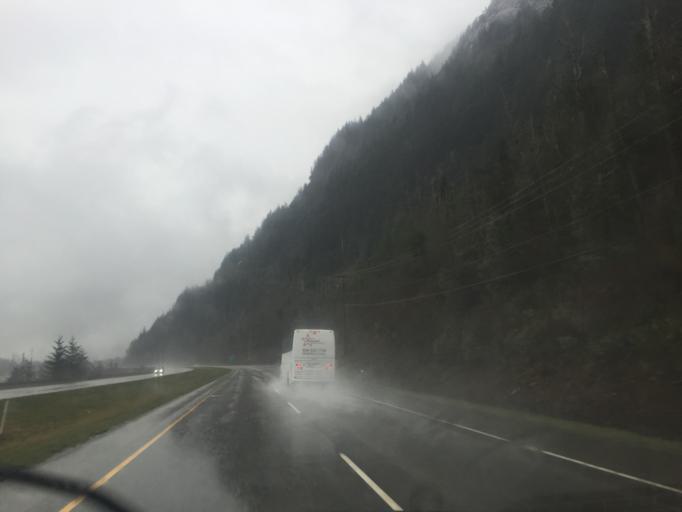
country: CA
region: British Columbia
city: Hope
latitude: 49.3641
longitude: -121.5442
